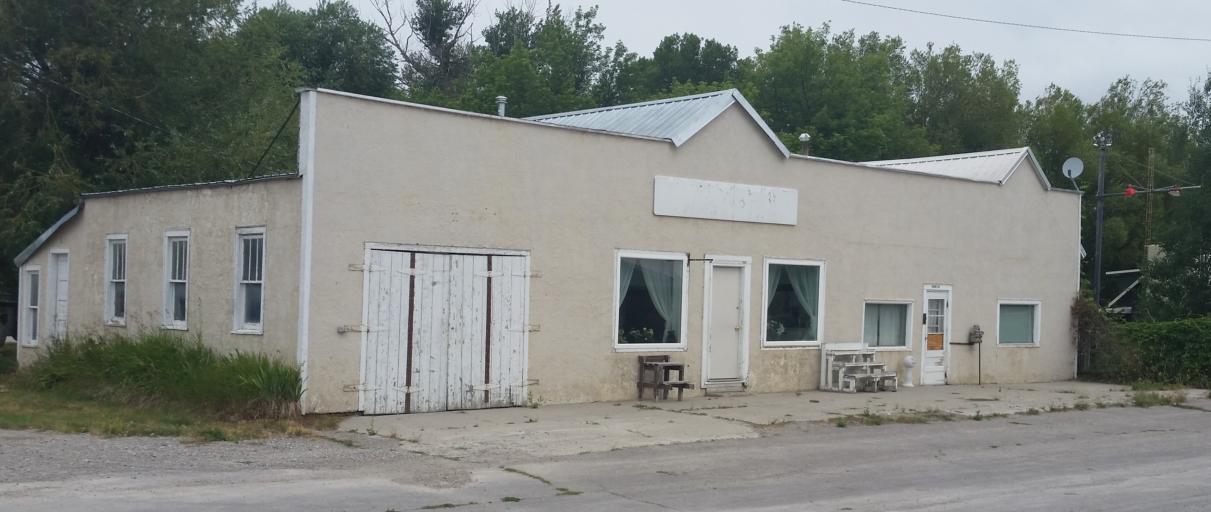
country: US
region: Montana
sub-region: Glacier County
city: Cut Bank
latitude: 48.1907
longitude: -112.5009
